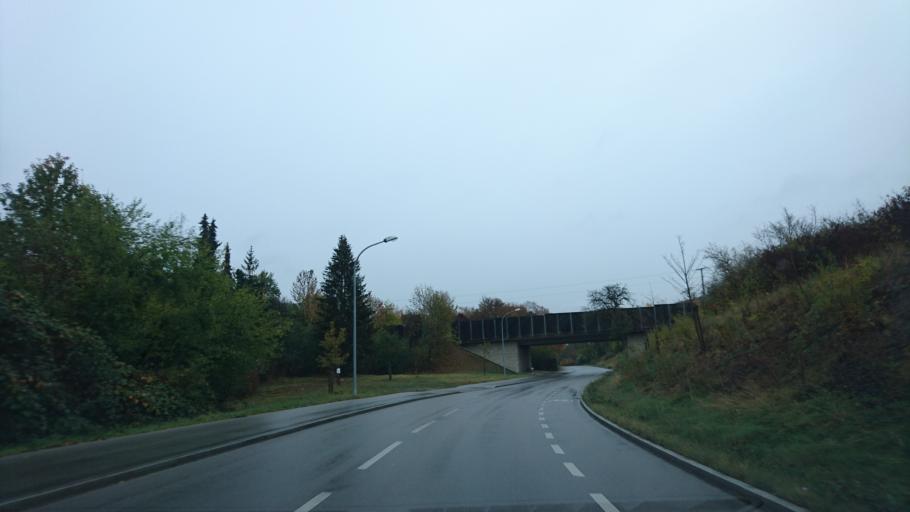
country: DE
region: Bavaria
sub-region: Regierungsbezirk Mittelfranken
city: Weissenburg in Bayern
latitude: 49.0397
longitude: 10.9802
